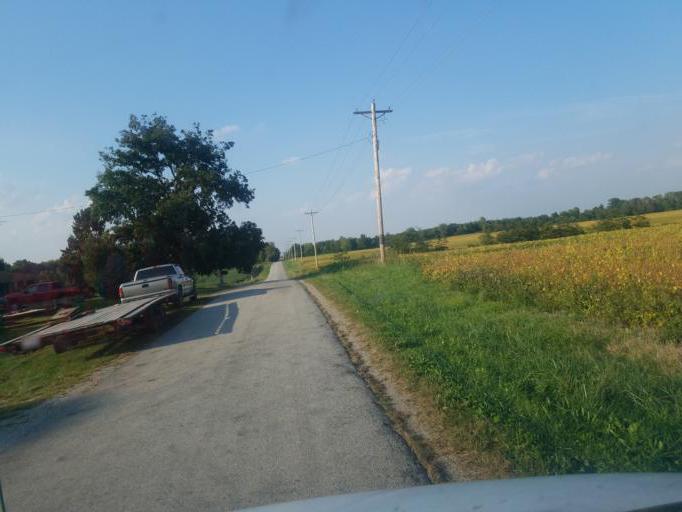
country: US
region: Ohio
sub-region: Seneca County
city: Tiffin
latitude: 40.9423
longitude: -83.1124
